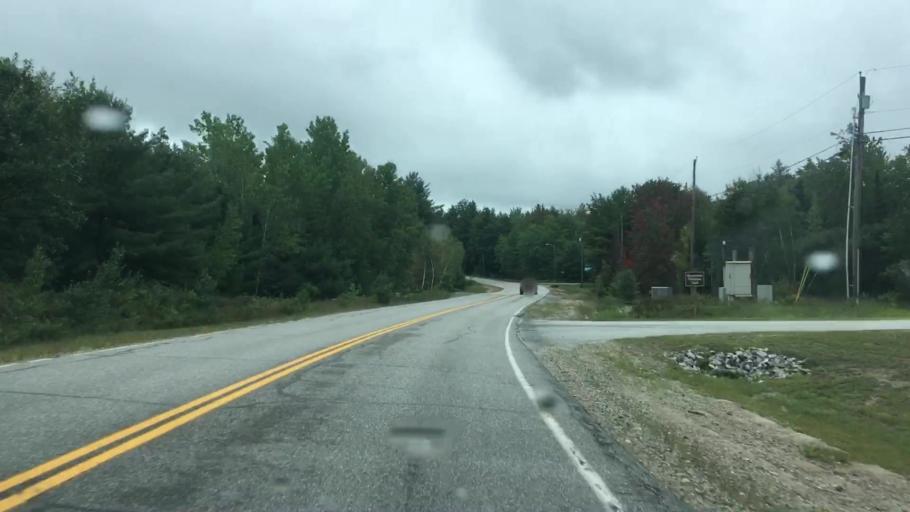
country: US
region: Maine
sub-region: Oxford County
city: Brownfield
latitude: 43.9860
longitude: -70.9323
